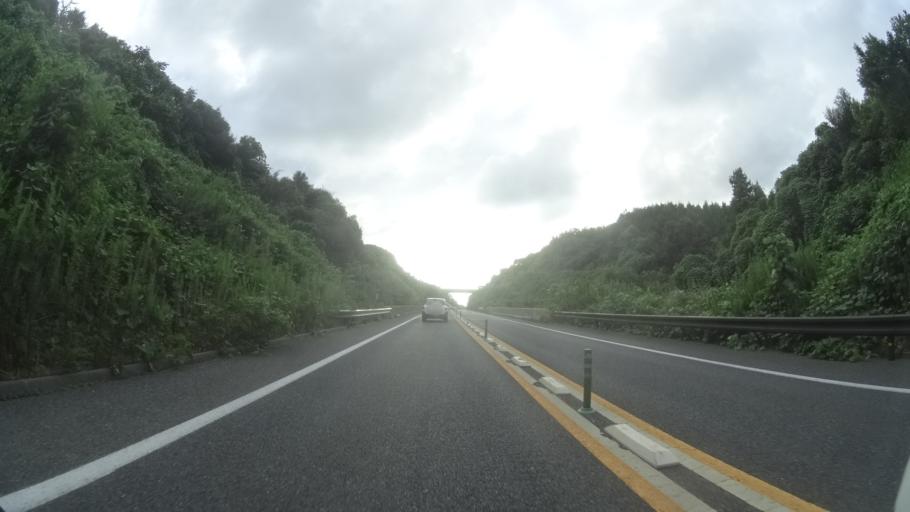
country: JP
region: Tottori
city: Kurayoshi
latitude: 35.5073
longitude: 133.6126
